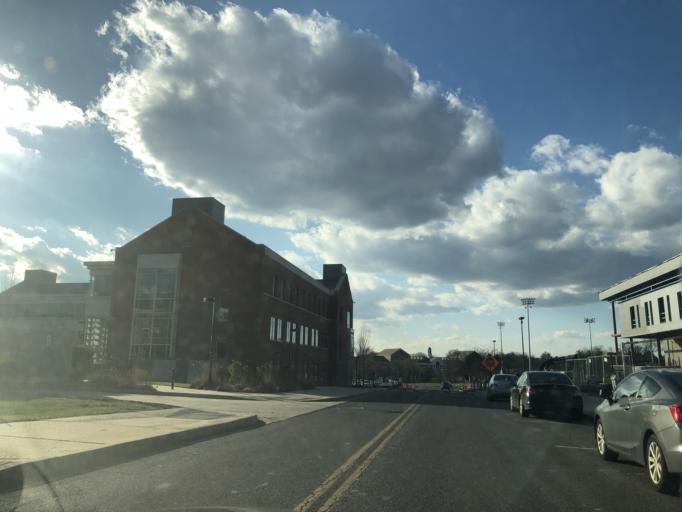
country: US
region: Maryland
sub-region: Prince George's County
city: College Park
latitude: 38.9872
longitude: -76.9476
